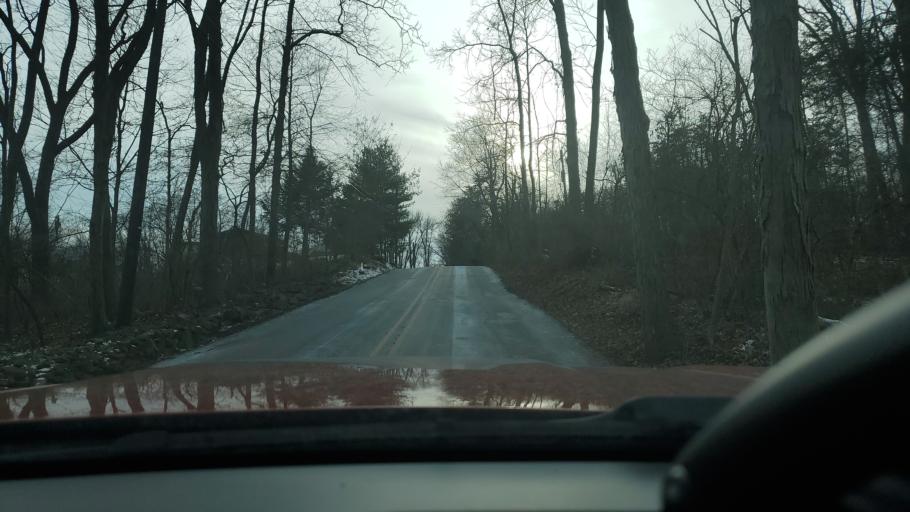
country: US
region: Pennsylvania
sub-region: Montgomery County
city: Red Hill
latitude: 40.3245
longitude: -75.5162
